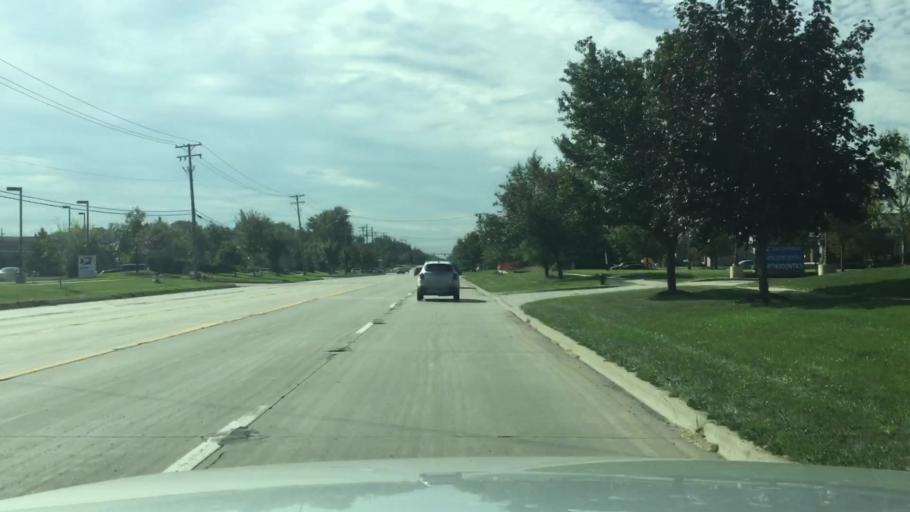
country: US
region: Michigan
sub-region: Wayne County
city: Canton
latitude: 42.3101
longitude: -83.4874
